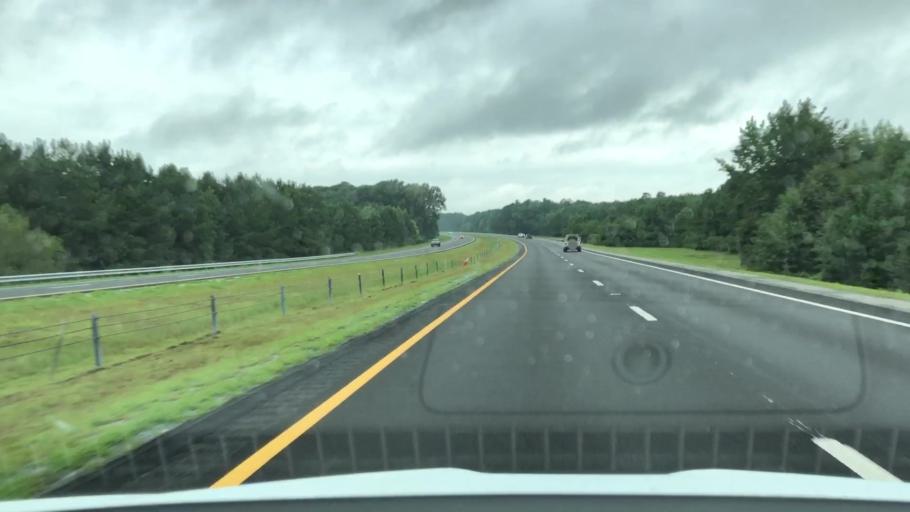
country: US
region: North Carolina
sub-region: Wayne County
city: Fremont
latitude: 35.4725
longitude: -77.9870
